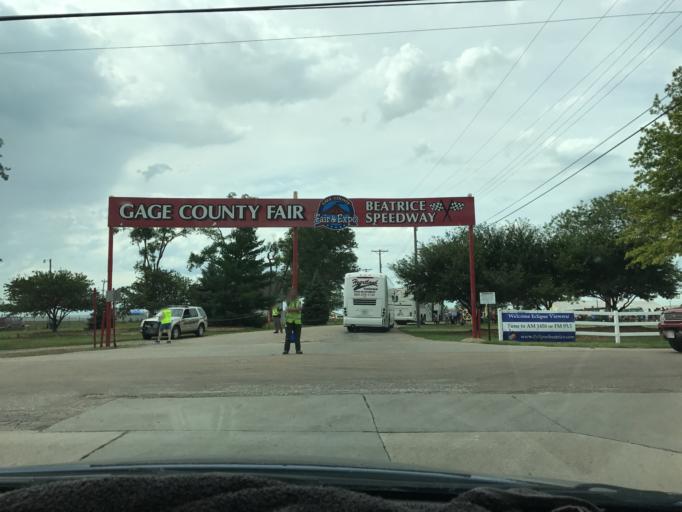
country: US
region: Nebraska
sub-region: Gage County
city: Beatrice
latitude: 40.2631
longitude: -96.7787
